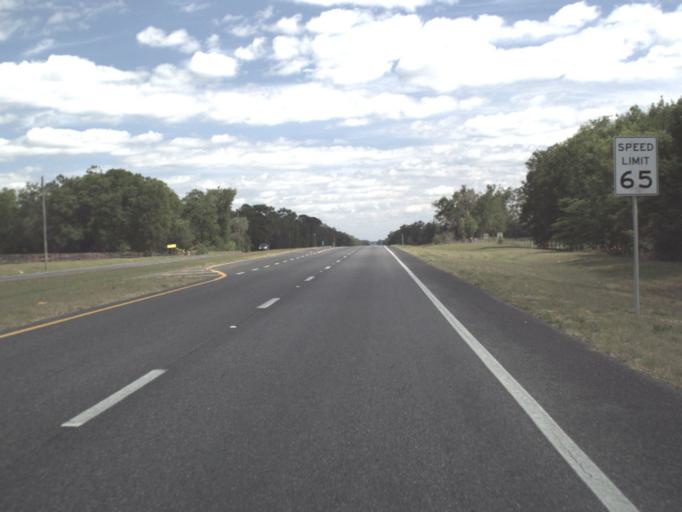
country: US
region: Florida
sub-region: Levy County
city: Williston
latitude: 29.3534
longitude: -82.3988
